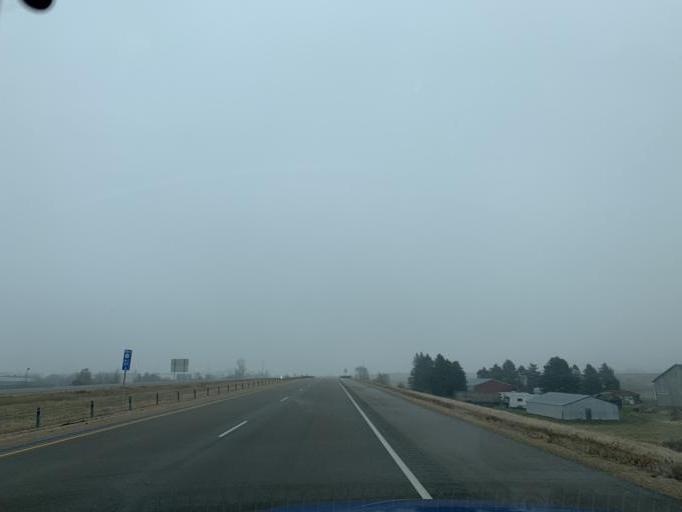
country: US
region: Wisconsin
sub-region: Dane County
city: Sun Prairie
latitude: 43.1998
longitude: -89.2011
